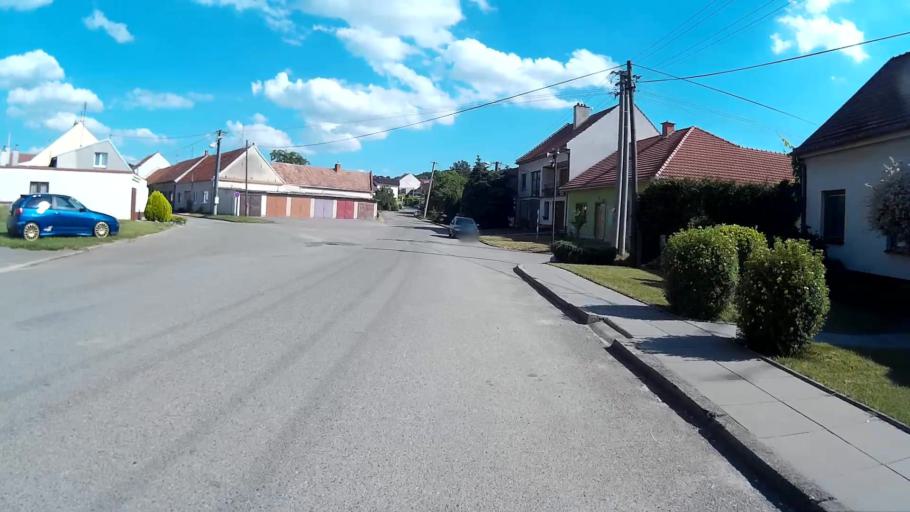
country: CZ
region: South Moravian
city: Krepice
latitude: 49.0028
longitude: 16.7171
